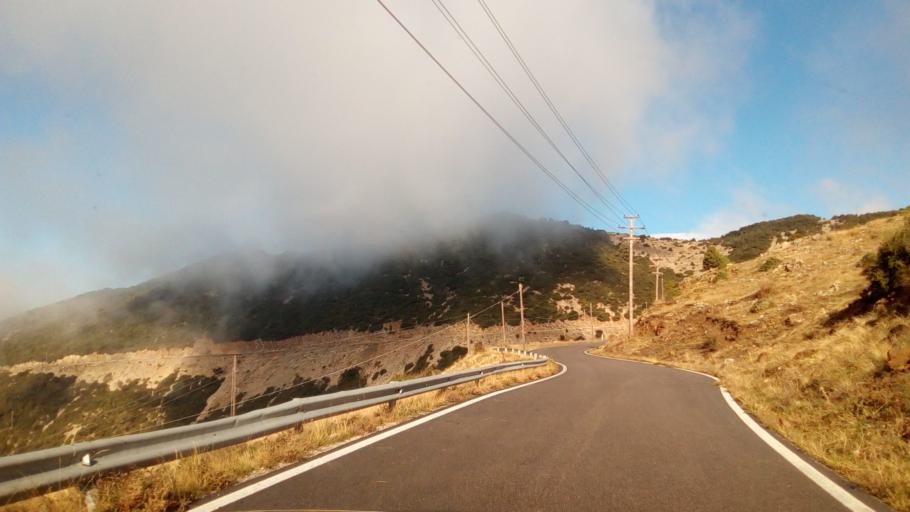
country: GR
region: West Greece
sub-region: Nomos Aitolias kai Akarnanias
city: Thermo
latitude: 38.5842
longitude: 21.7738
